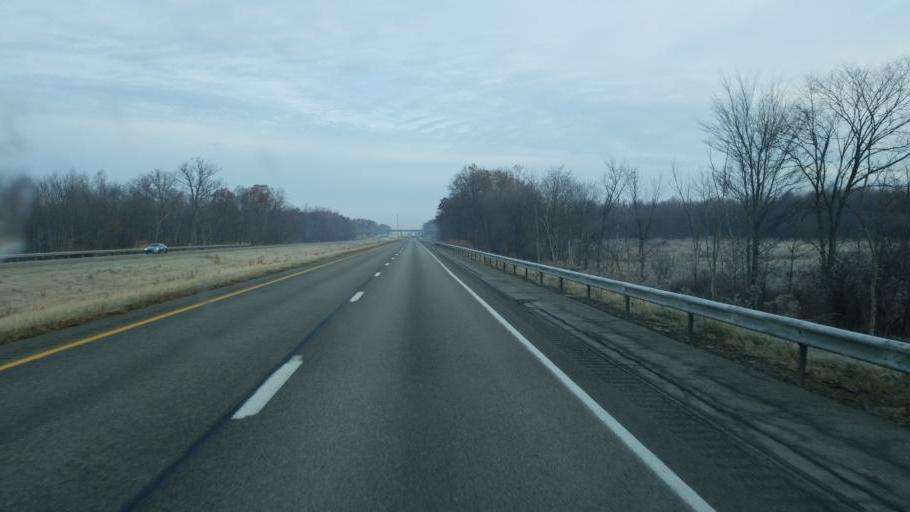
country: US
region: Pennsylvania
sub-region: Mercer County
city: Stoneboro
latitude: 41.3258
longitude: -80.1594
